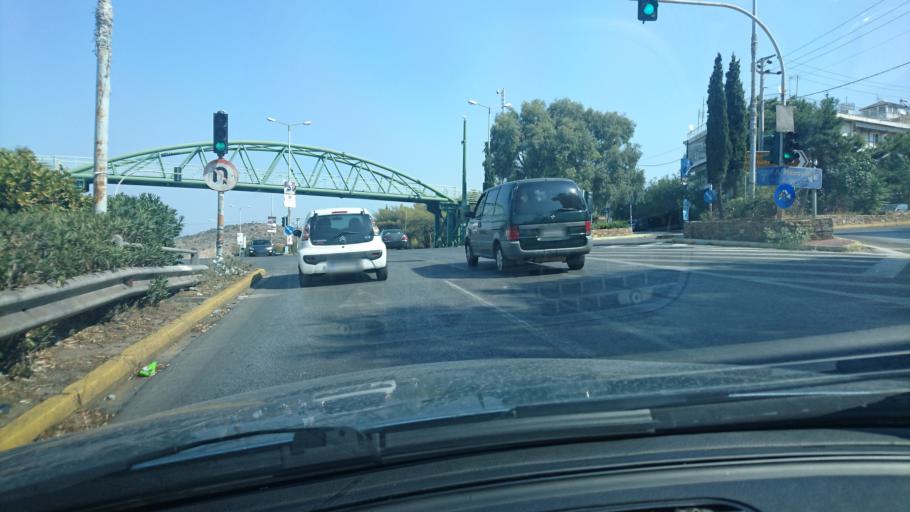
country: GR
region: Attica
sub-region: Nomarchia Athinas
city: Kaisariani
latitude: 37.9489
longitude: 23.7681
